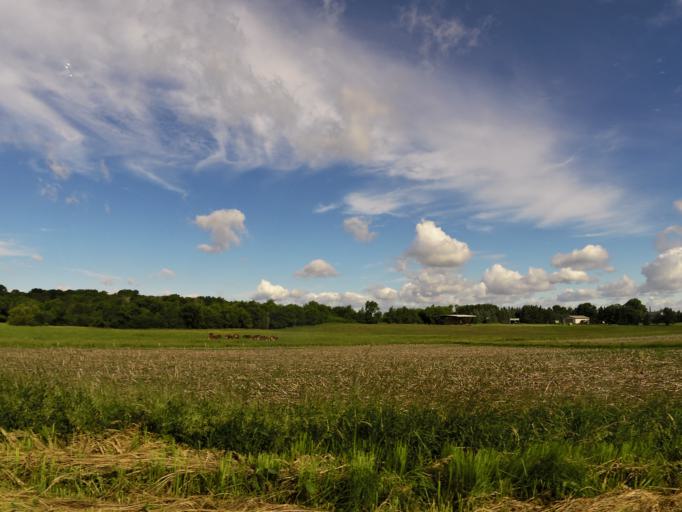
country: US
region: Minnesota
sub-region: Goodhue County
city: Cannon Falls
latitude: 44.6122
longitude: -92.9777
